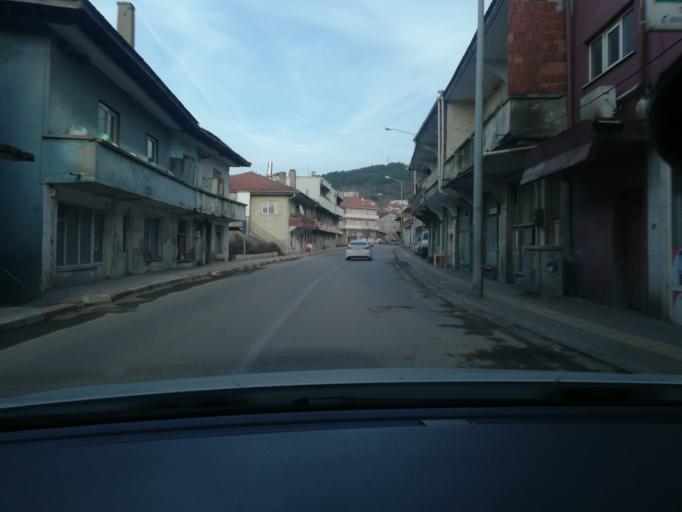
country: TR
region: Zonguldak
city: Tieum
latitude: 41.5613
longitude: 32.0257
